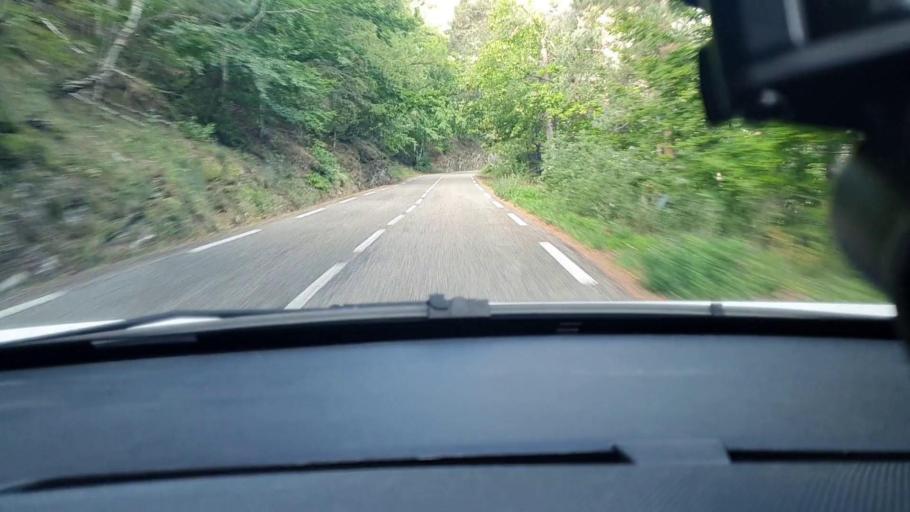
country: FR
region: Rhone-Alpes
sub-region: Departement de l'Ardeche
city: Les Vans
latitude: 44.4289
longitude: 4.0028
